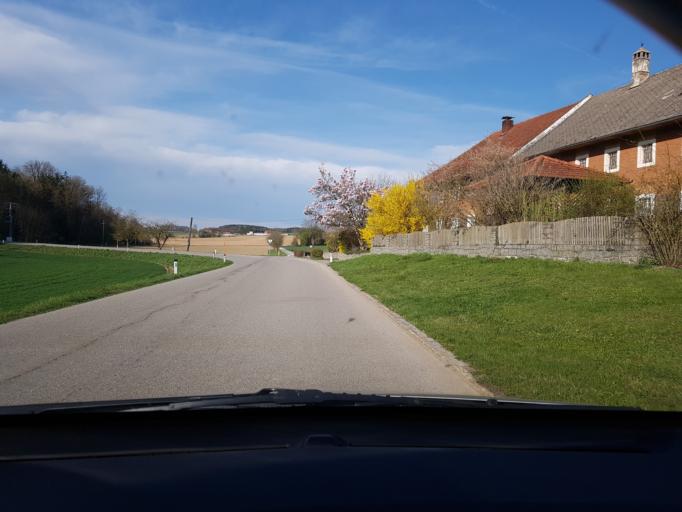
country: AT
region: Upper Austria
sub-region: Politischer Bezirk Linz-Land
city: Sankt Florian
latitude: 48.1558
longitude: 14.3869
